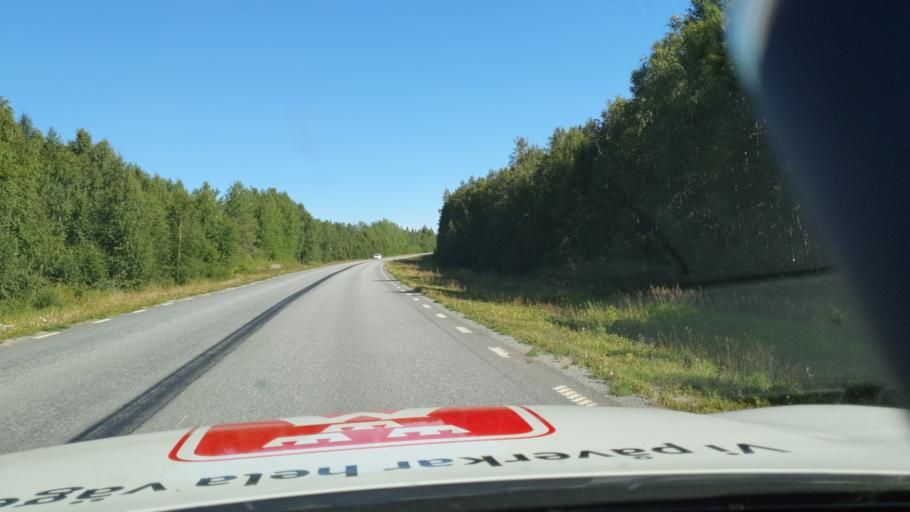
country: SE
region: Vaesterbotten
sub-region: Dorotea Kommun
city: Dorotea
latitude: 64.3466
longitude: 16.6561
